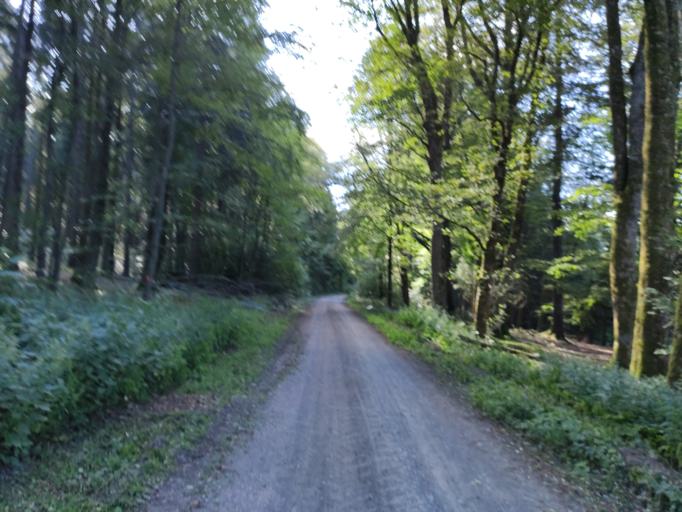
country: DE
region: Thuringia
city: Wurzbach
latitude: 50.4201
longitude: 11.5340
